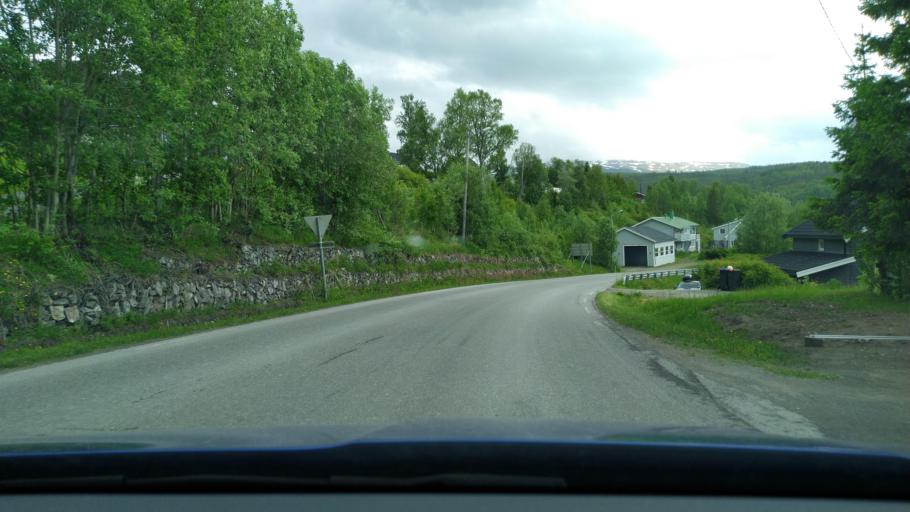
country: NO
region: Troms
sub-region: Salangen
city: Sjovegan
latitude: 68.8719
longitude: 17.8541
